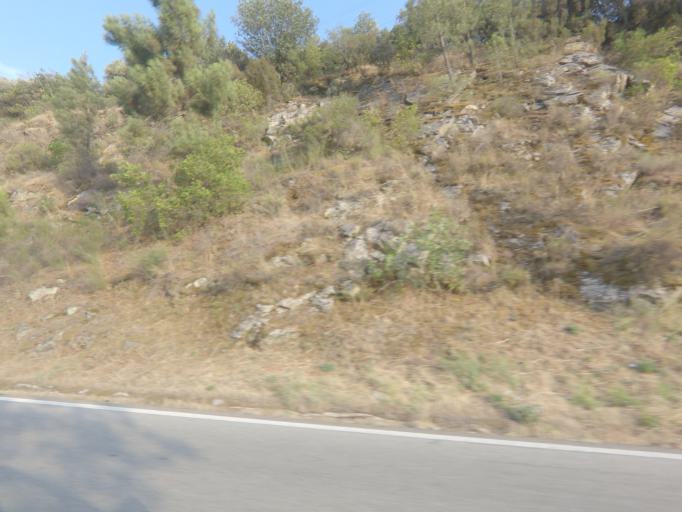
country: PT
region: Viseu
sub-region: Armamar
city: Armamar
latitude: 41.1409
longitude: -7.6974
